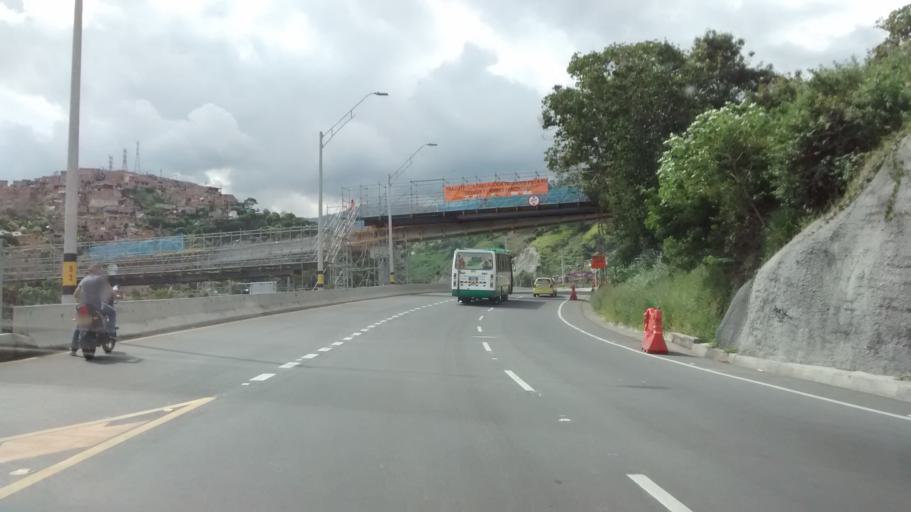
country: CO
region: Antioquia
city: Medellin
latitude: 6.2762
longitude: -75.6039
